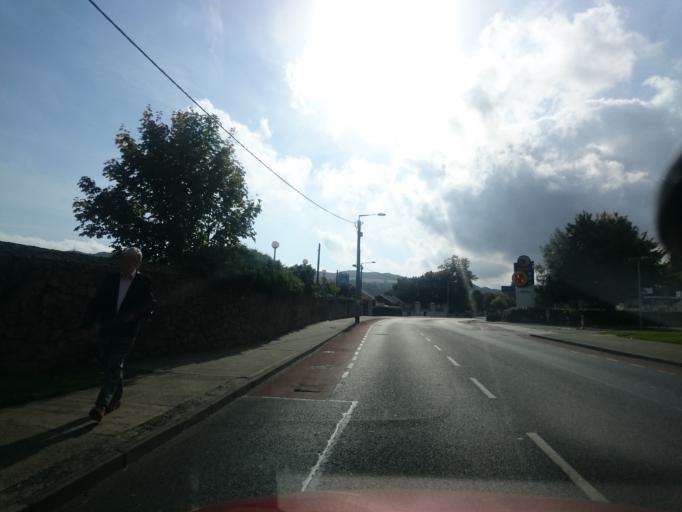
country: IE
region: Leinster
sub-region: Wicklow
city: Bray
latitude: 53.1963
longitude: -6.1078
